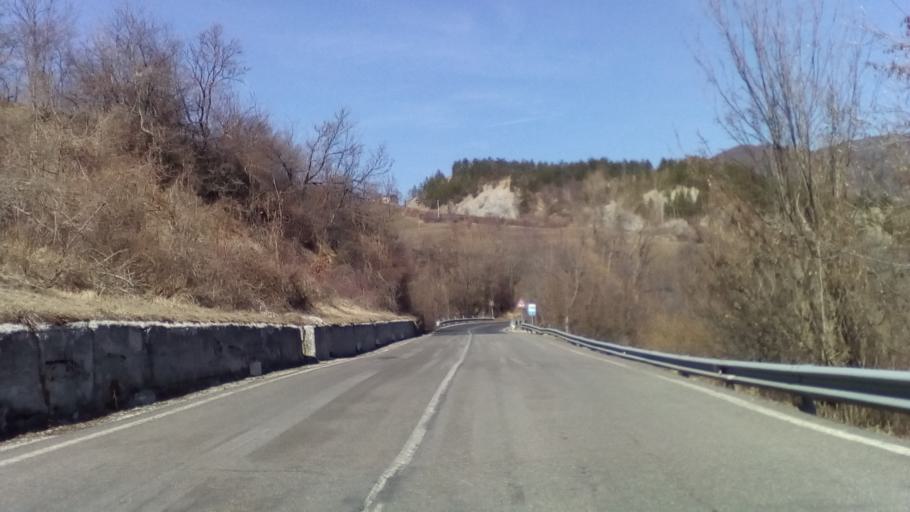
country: IT
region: Emilia-Romagna
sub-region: Provincia di Modena
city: Riolunato
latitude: 44.2436
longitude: 10.6335
